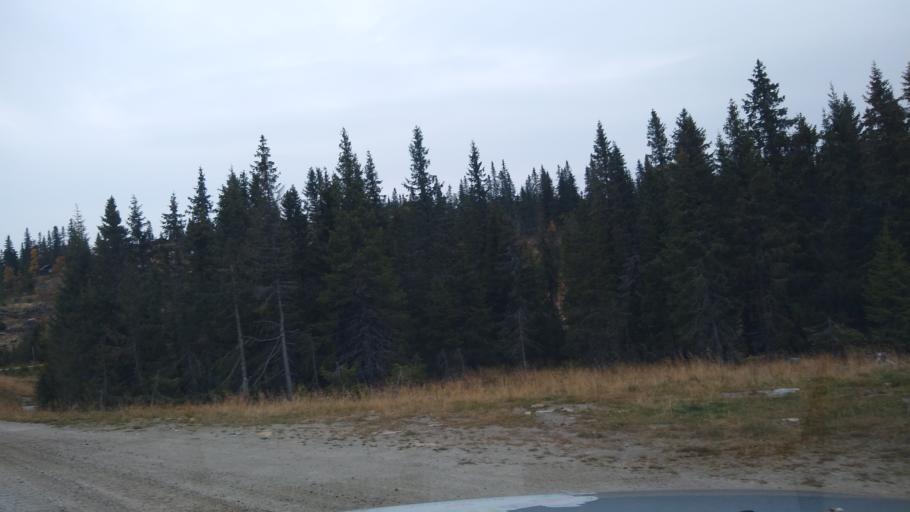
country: NO
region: Oppland
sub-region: Ringebu
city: Ringebu
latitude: 61.4725
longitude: 10.1347
